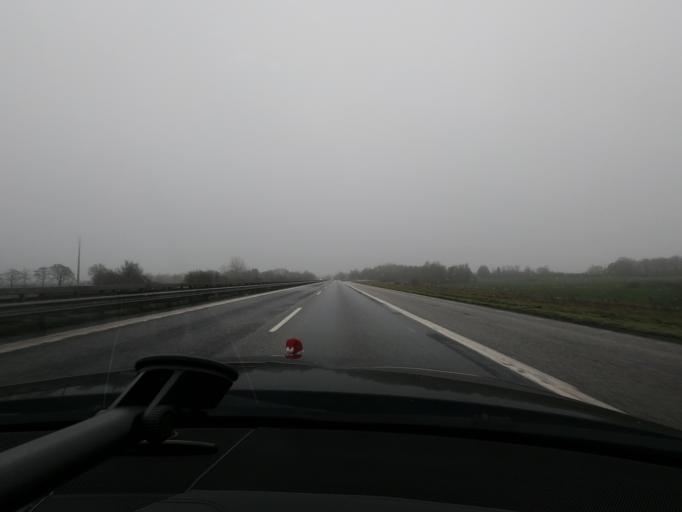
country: DE
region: Schleswig-Holstein
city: Lottorf
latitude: 54.4324
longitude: 9.5954
